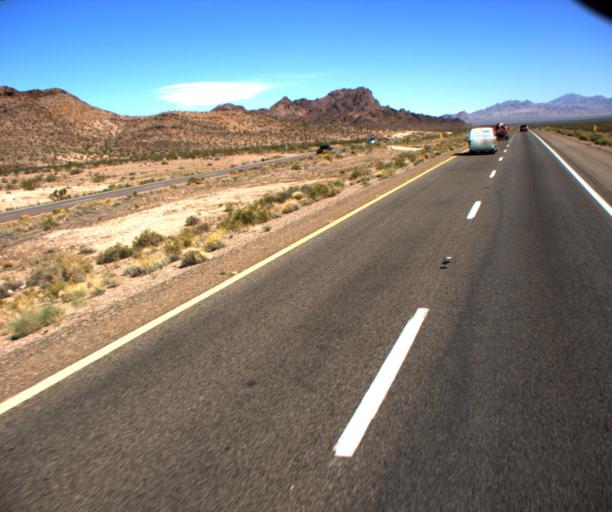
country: US
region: Arizona
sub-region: Mohave County
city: Dolan Springs
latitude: 35.7616
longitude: -114.5077
